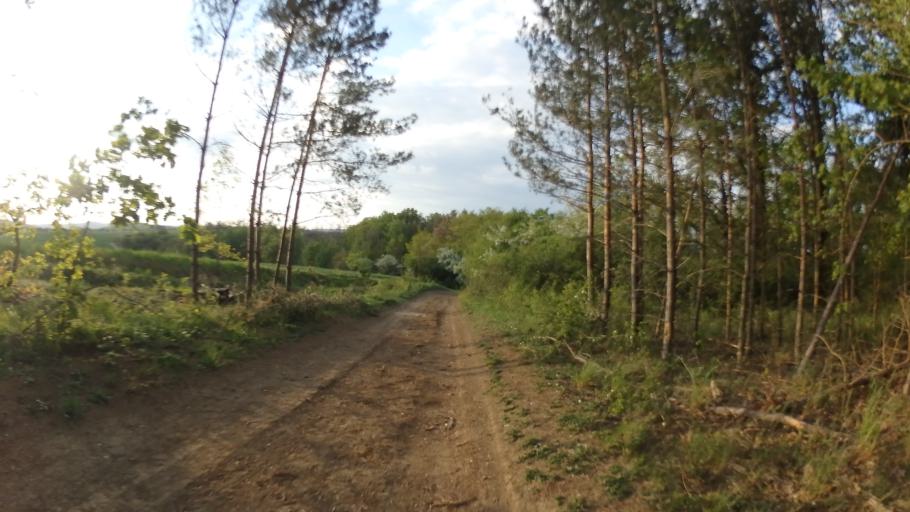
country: CZ
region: South Moravian
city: Moravany
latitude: 49.1368
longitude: 16.5648
